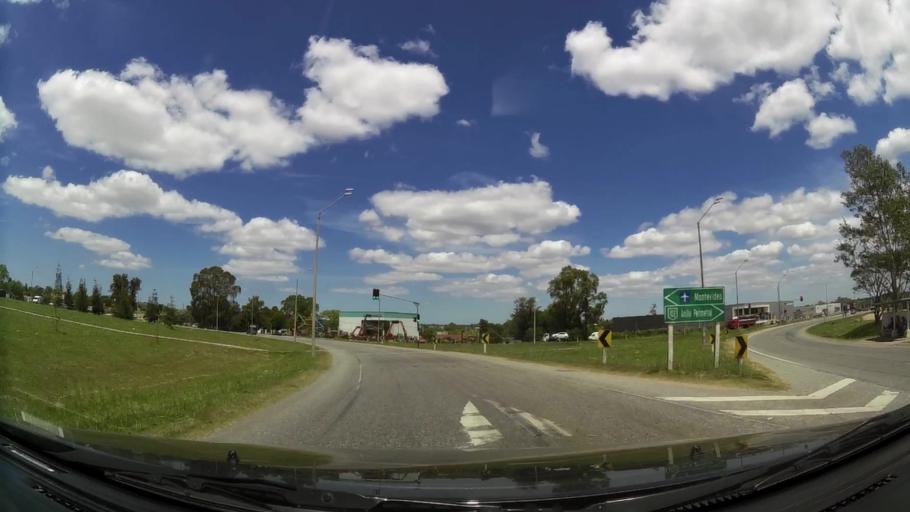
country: UY
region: Canelones
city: Colonia Nicolich
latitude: -34.8191
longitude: -56.0091
